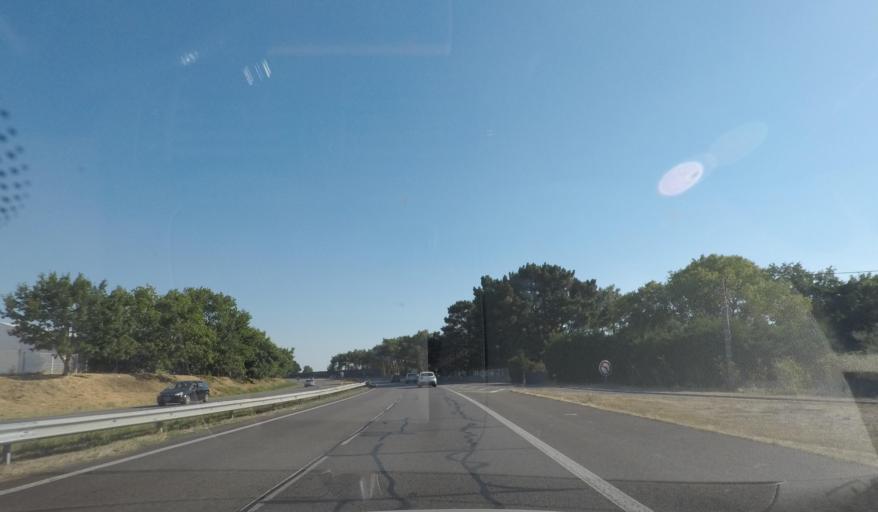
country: FR
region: Pays de la Loire
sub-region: Departement de la Loire-Atlantique
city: Saint-Brevin-les-Pins
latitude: 47.2438
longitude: -2.1602
